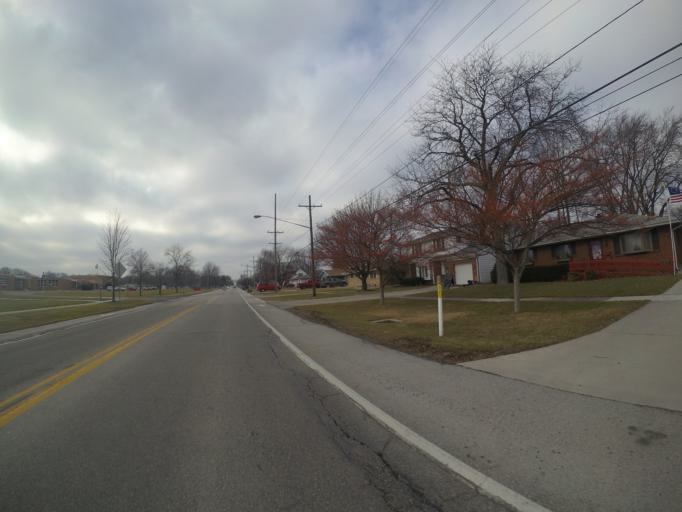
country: US
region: Ohio
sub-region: Lucas County
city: Oregon
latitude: 41.6443
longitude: -83.4685
